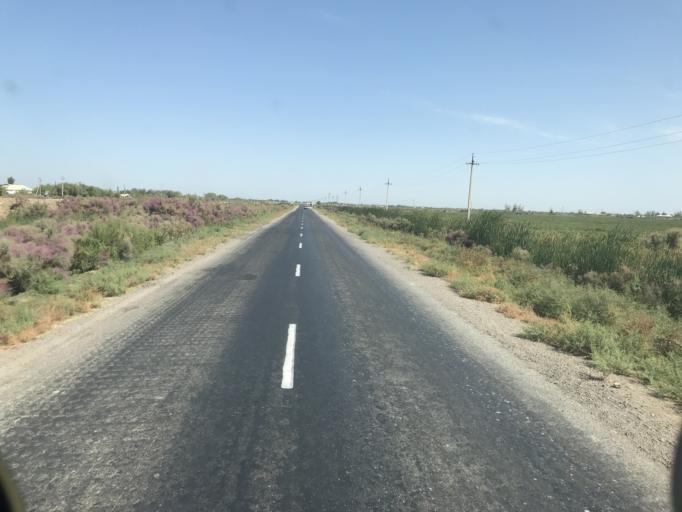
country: KZ
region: Ongtustik Qazaqstan
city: Myrzakent
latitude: 40.7351
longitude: 68.5367
